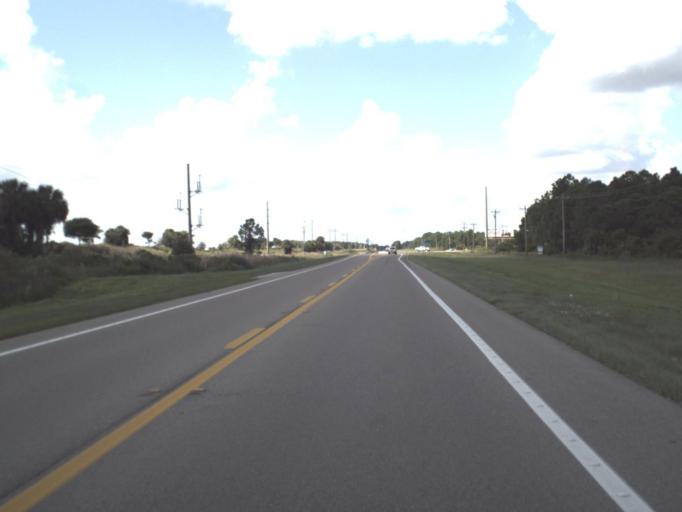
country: US
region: Florida
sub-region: Lee County
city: Lehigh Acres
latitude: 26.5281
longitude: -81.6017
